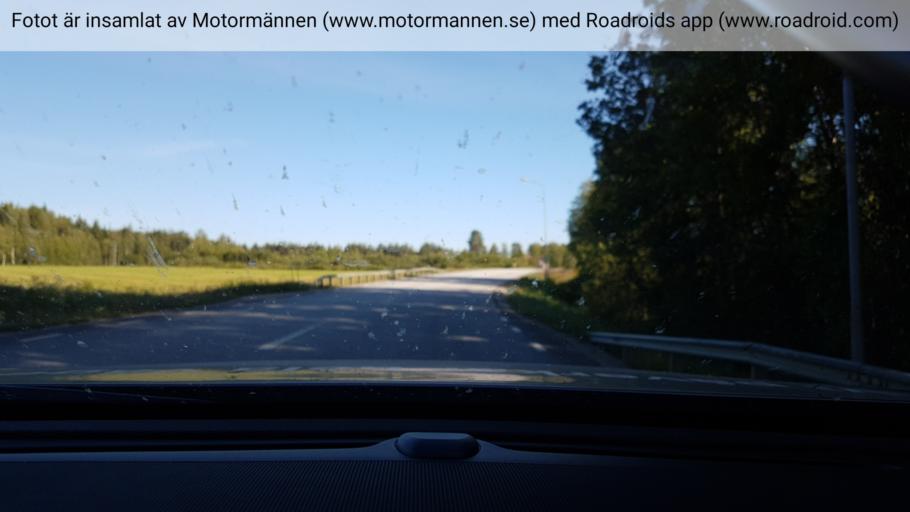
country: SE
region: Vaesterbotten
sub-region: Vindelns Kommun
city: Vindeln
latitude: 64.1231
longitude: 19.5594
